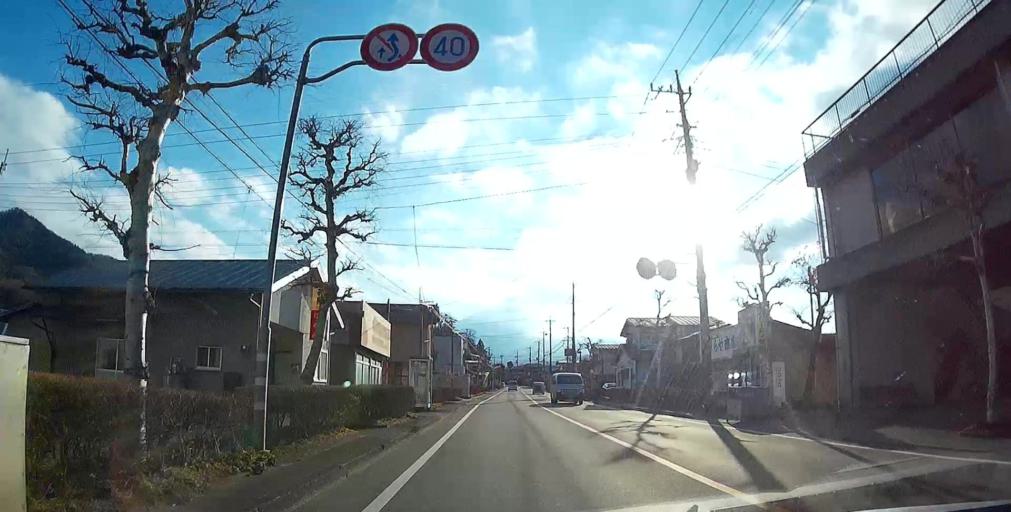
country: JP
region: Yamanashi
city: Fujikawaguchiko
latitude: 35.4867
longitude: 138.8201
